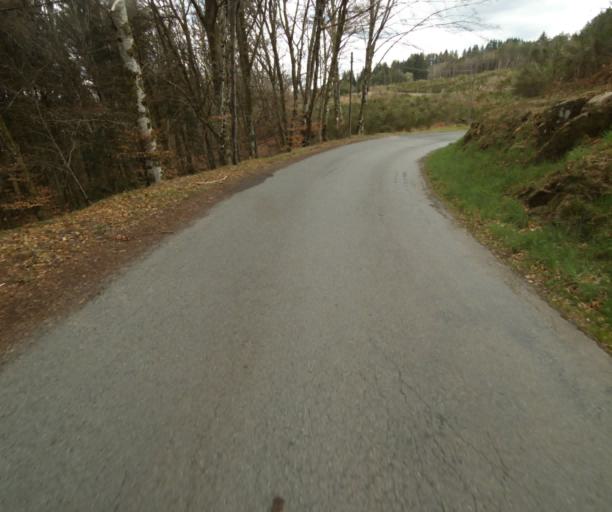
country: FR
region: Limousin
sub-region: Departement de la Correze
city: Correze
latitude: 45.3180
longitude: 1.9340
